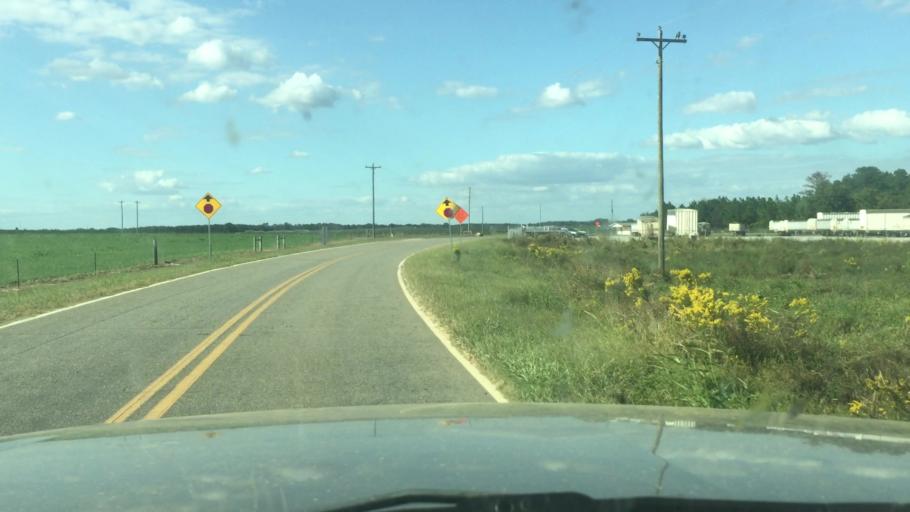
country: US
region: Georgia
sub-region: Terrell County
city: Dawson
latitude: 31.7639
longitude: -84.3535
